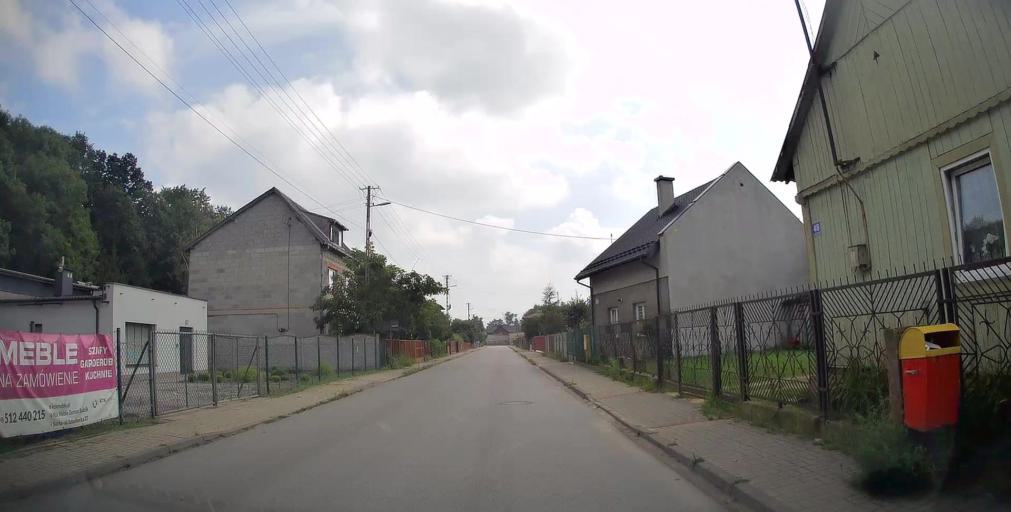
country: PL
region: Masovian Voivodeship
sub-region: Powiat bialobrzeski
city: Sucha
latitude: 51.6195
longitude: 20.9507
